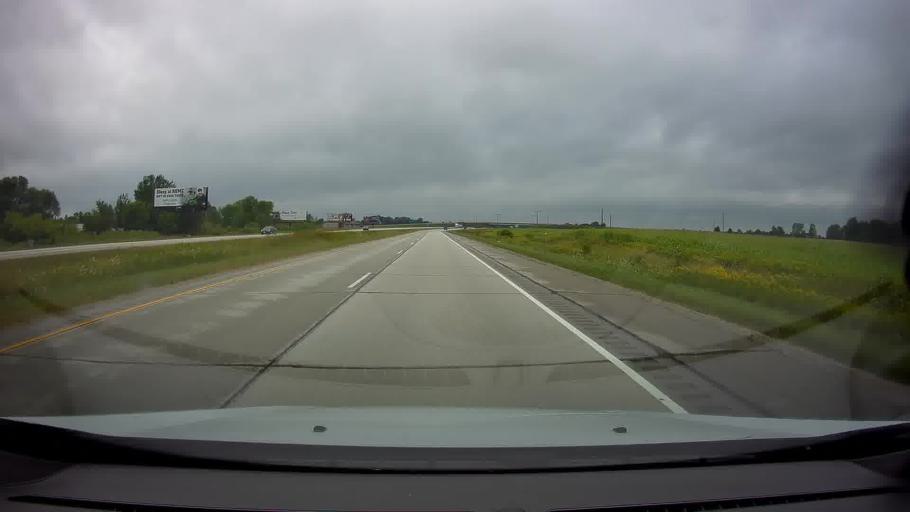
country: US
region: Wisconsin
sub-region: Brown County
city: Pulaski
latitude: 44.5998
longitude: -88.2386
